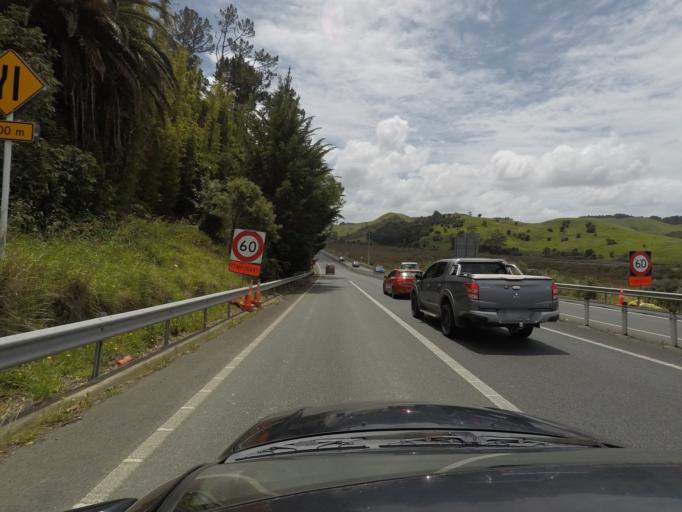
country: NZ
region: Auckland
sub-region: Auckland
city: Warkworth
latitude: -36.5293
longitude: 174.6777
